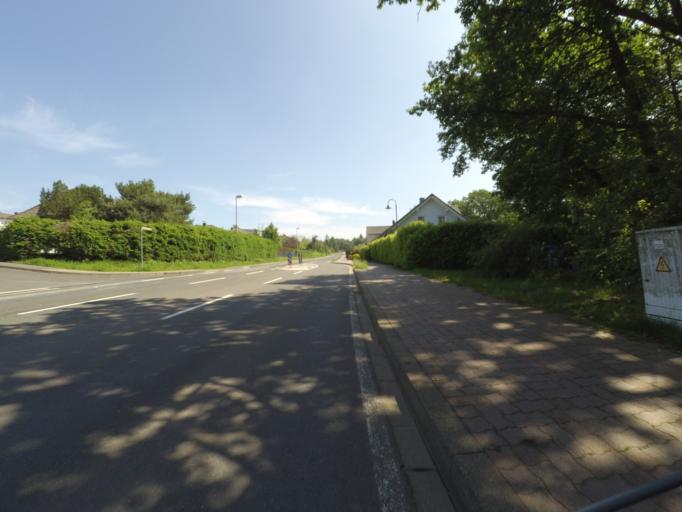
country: DE
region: Rheinland-Pfalz
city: Ney
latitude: 50.2107
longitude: 7.5367
